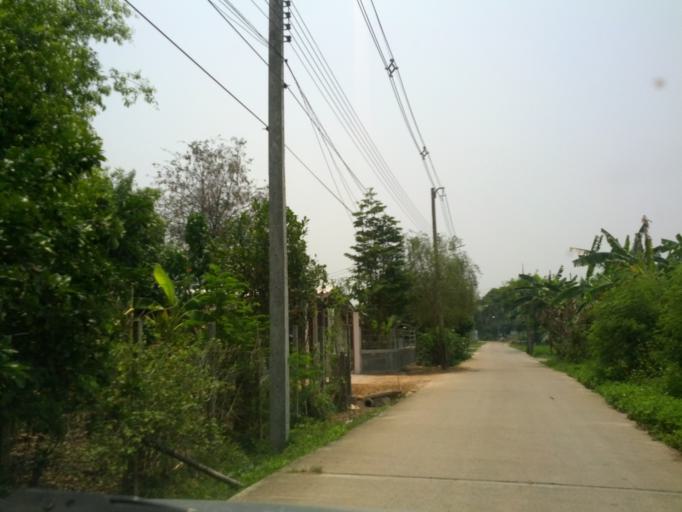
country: TH
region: Chiang Mai
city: San Sai
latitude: 18.8937
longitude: 99.0727
